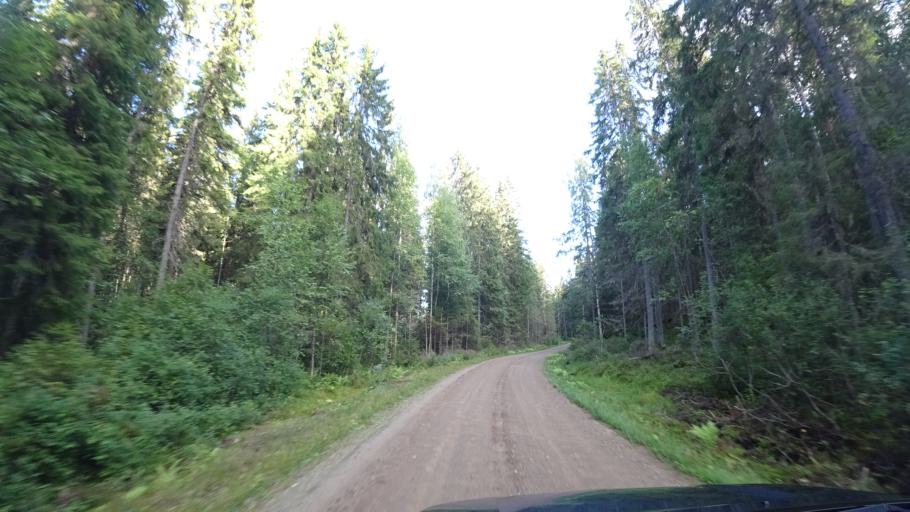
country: FI
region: Paijanne Tavastia
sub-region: Lahti
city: Auttoinen
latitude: 61.2213
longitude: 25.2023
